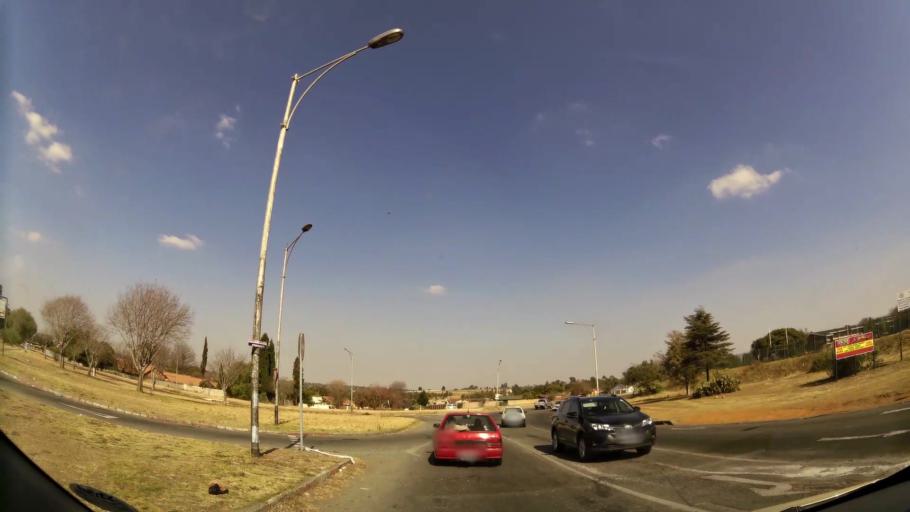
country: ZA
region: Gauteng
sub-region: West Rand District Municipality
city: Krugersdorp
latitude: -26.1217
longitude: 27.8171
